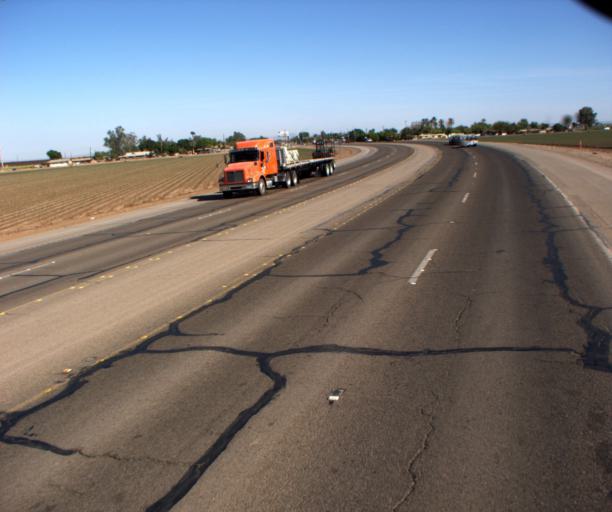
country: US
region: Arizona
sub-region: Yuma County
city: San Luis
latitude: 32.5492
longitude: -114.7854
